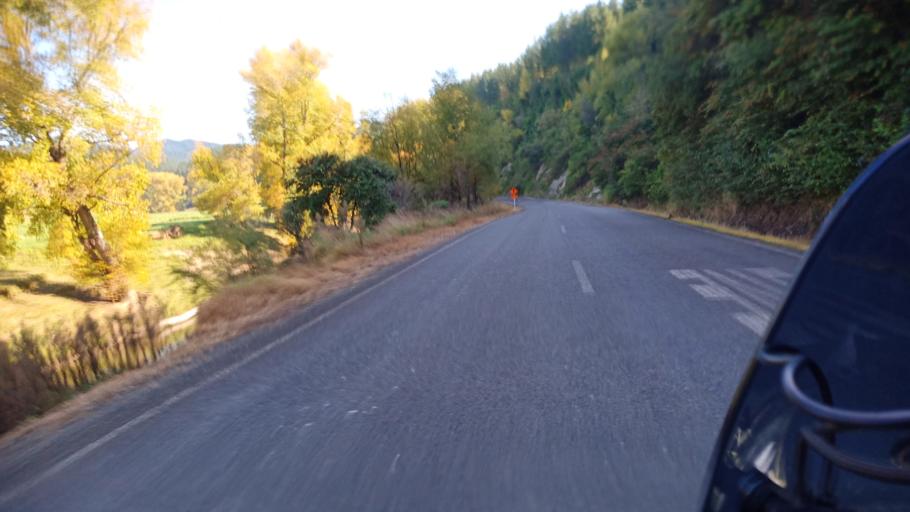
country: NZ
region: Hawke's Bay
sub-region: Wairoa District
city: Wairoa
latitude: -38.9227
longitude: 177.2603
